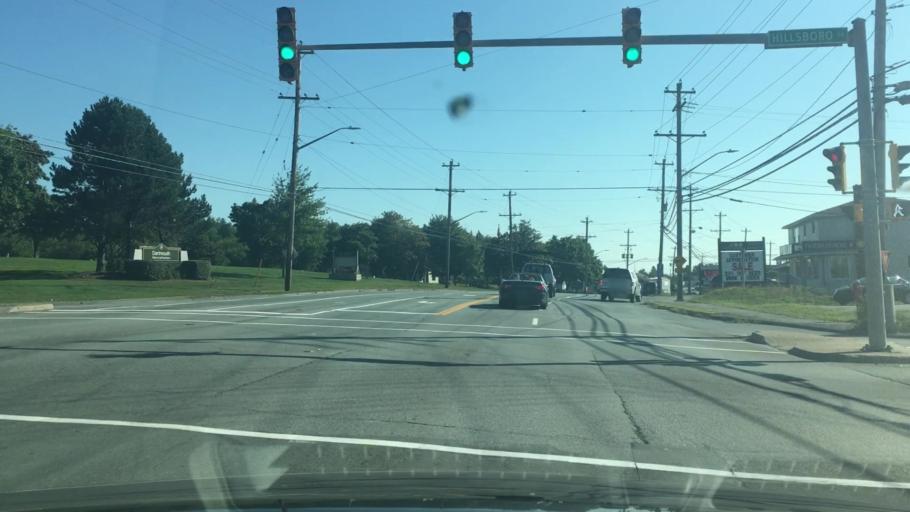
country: CA
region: Nova Scotia
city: Cole Harbour
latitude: 44.6980
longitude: -63.4931
